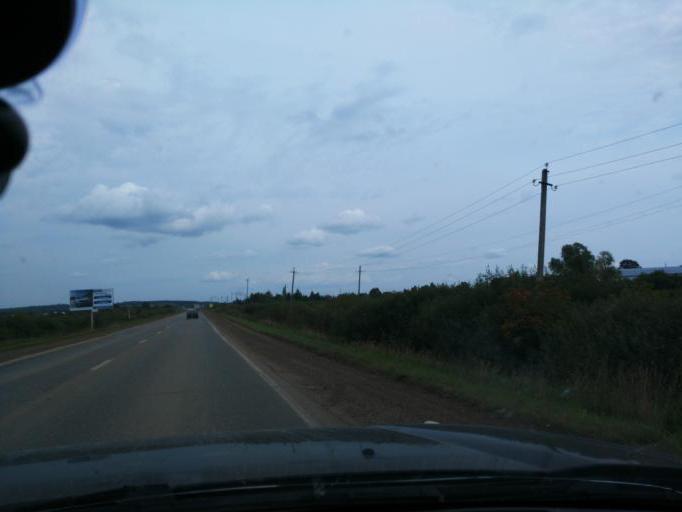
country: RU
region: Perm
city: Kuyeda
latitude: 56.4460
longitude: 55.5919
